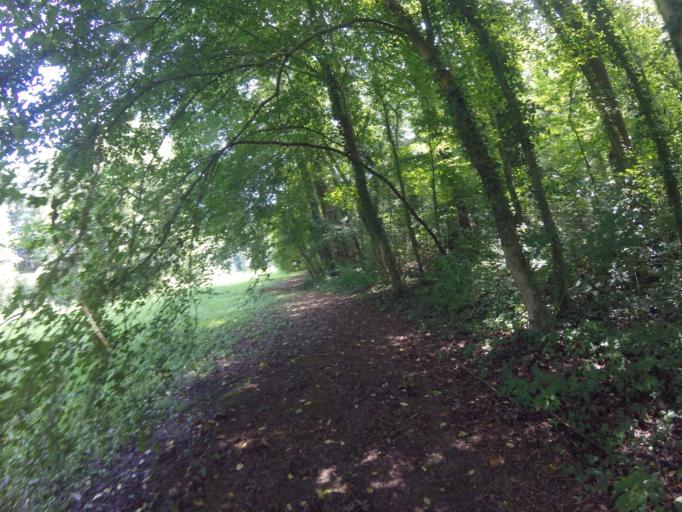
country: HU
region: Zala
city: Letenye
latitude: 46.5093
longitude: 16.7022
